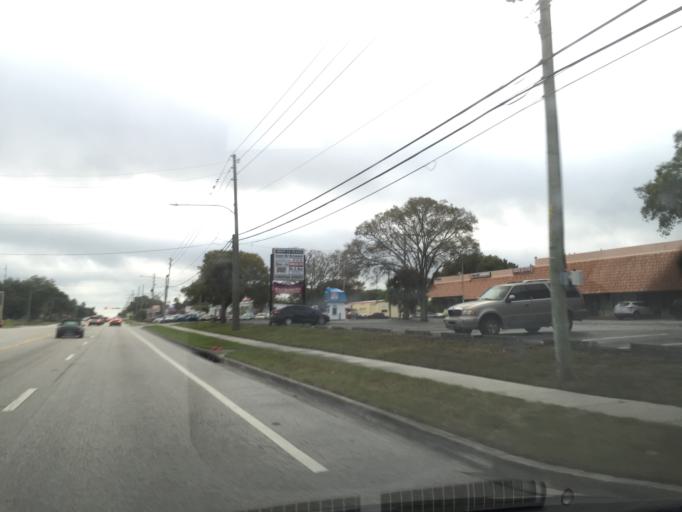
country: US
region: Florida
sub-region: Pinellas County
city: Clearwater
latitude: 27.9679
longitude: -82.7496
